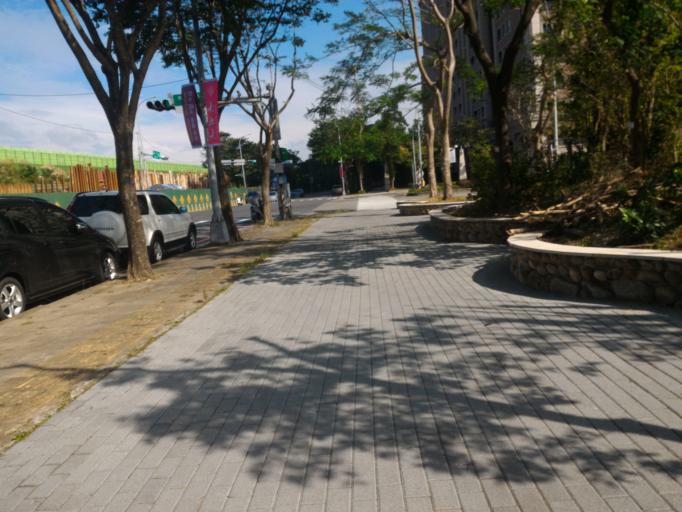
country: TW
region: Taiwan
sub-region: Taoyuan
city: Taoyuan
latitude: 24.9494
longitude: 121.3756
